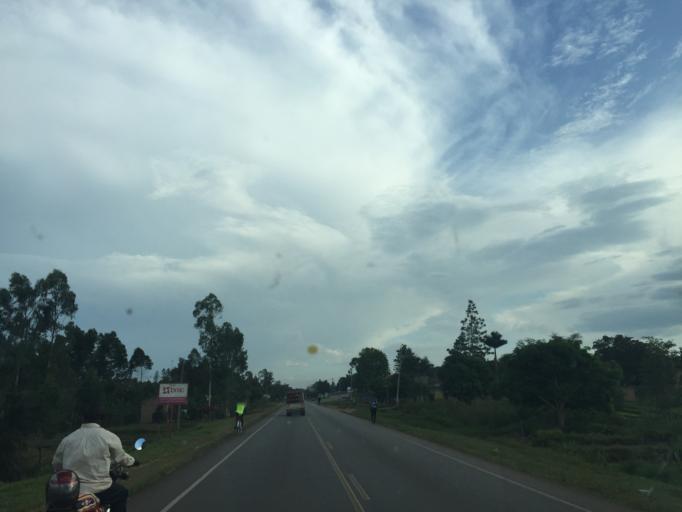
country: UG
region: Central Region
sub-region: Luwero District
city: Luwero
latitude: 0.8652
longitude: 32.4856
